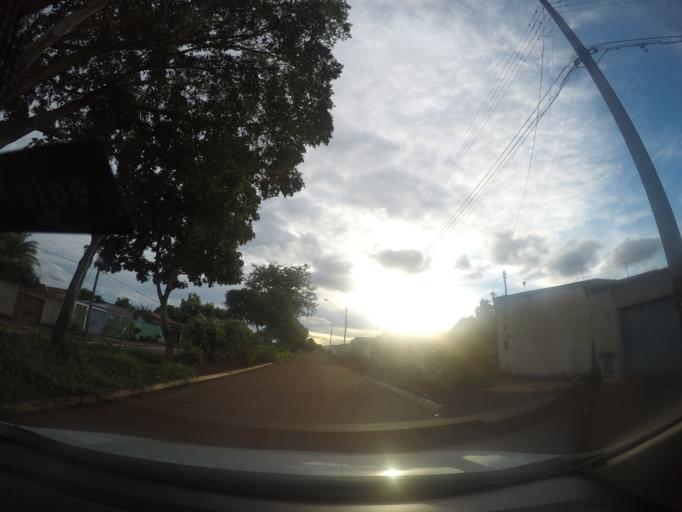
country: BR
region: Goias
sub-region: Goianira
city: Goianira
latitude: -16.5868
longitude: -49.3690
